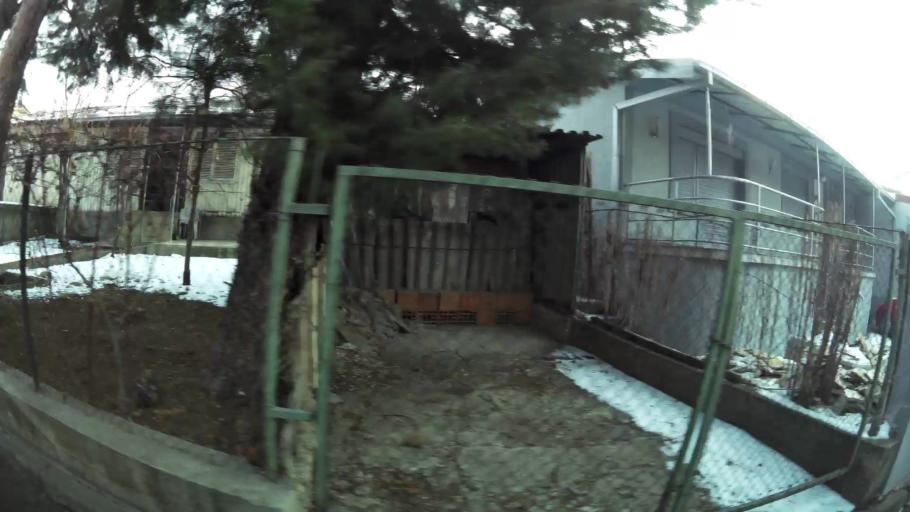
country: MK
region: Butel
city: Butel
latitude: 42.0222
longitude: 21.4505
